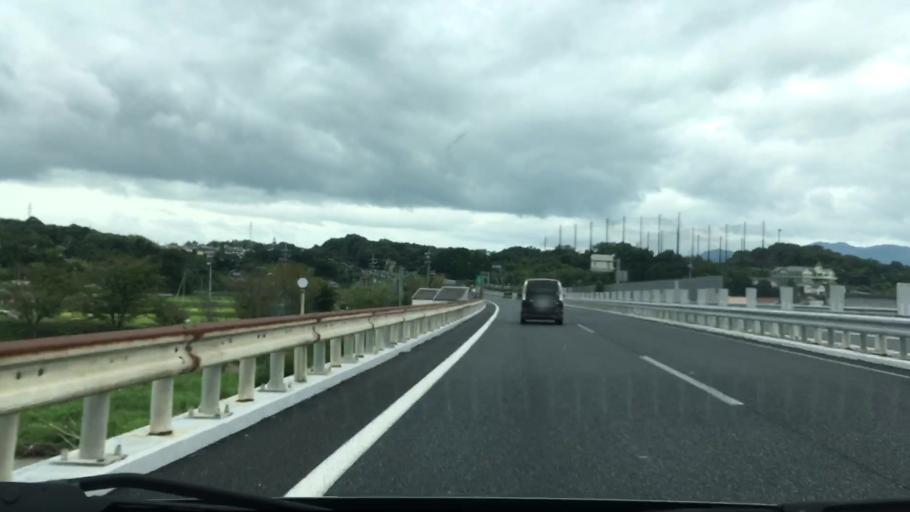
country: JP
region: Okayama
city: Tsuyama
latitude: 35.0667
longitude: 134.0460
